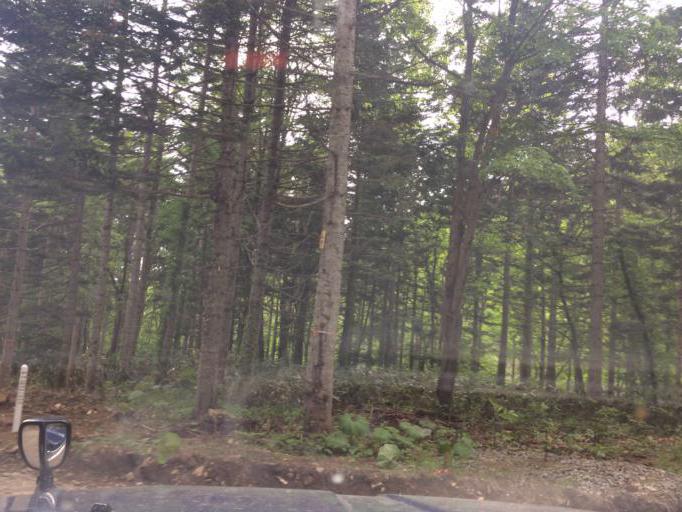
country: JP
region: Hokkaido
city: Niseko Town
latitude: 42.6541
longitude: 140.5059
